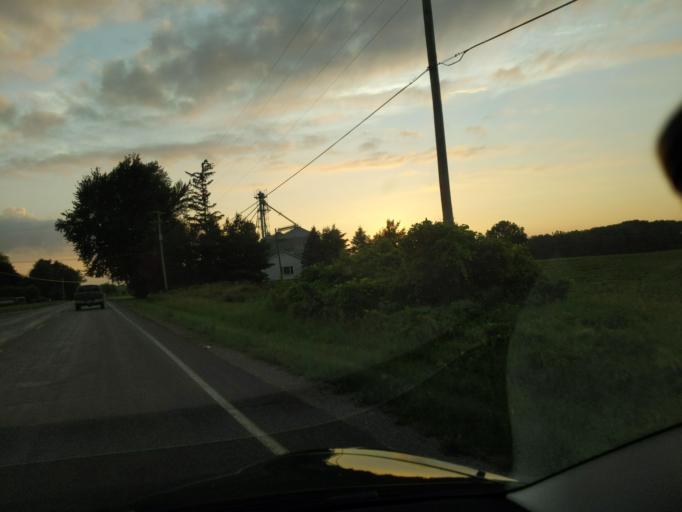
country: US
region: Michigan
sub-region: Ingham County
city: Mason
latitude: 42.5241
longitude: -84.4340
